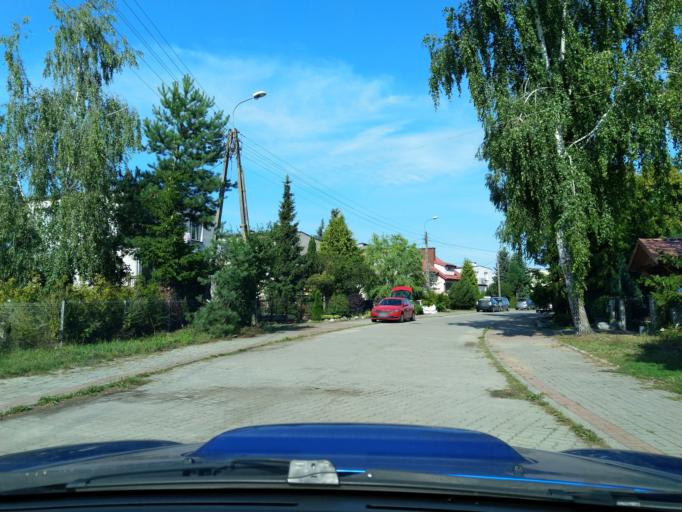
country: PL
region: Warmian-Masurian Voivodeship
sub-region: Olsztyn
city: Kortowo
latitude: 53.7640
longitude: 20.4245
